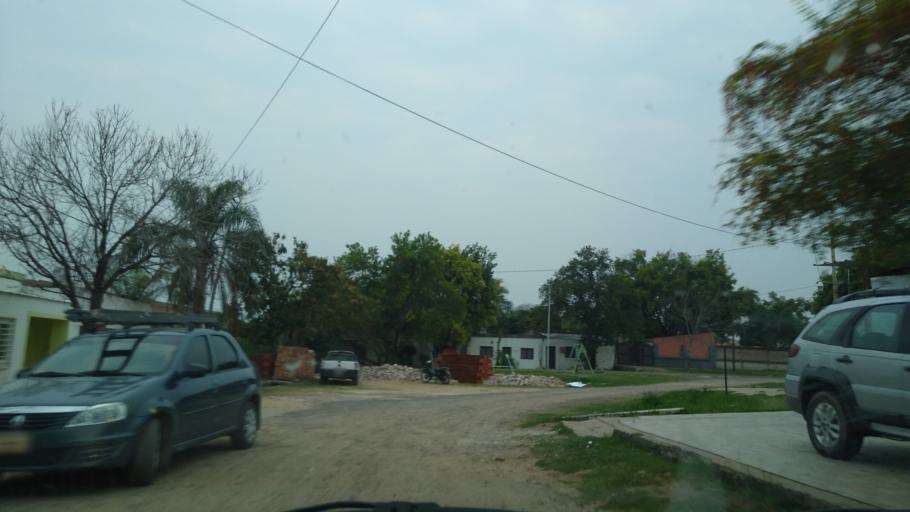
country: AR
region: Chaco
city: Barranqueras
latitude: -27.4773
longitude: -58.9523
